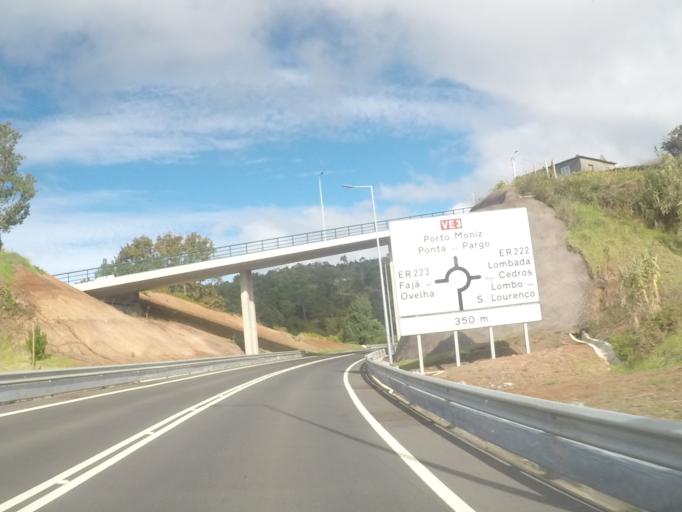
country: PT
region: Madeira
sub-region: Calheta
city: Faja da Ovelha
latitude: 32.7736
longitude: -17.2196
